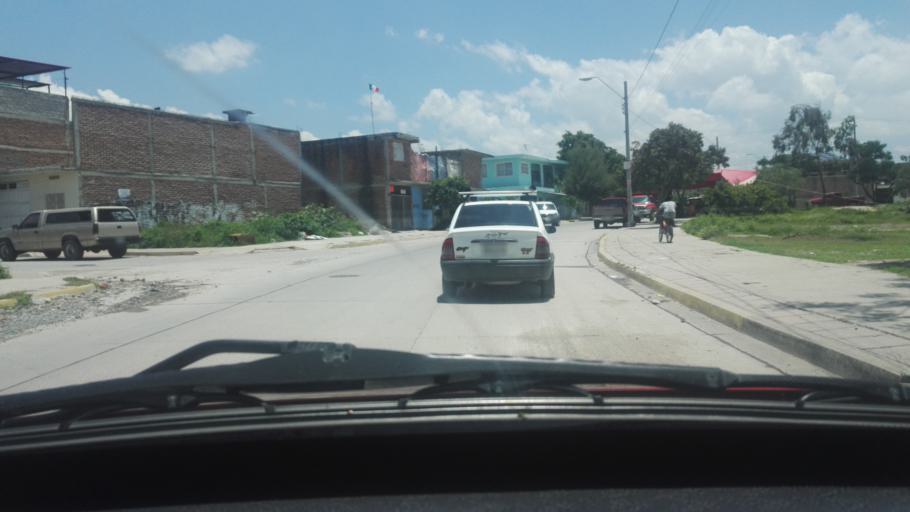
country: MX
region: Guanajuato
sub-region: Leon
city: San Jose de Duran (Los Troncoso)
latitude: 21.0807
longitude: -101.6351
